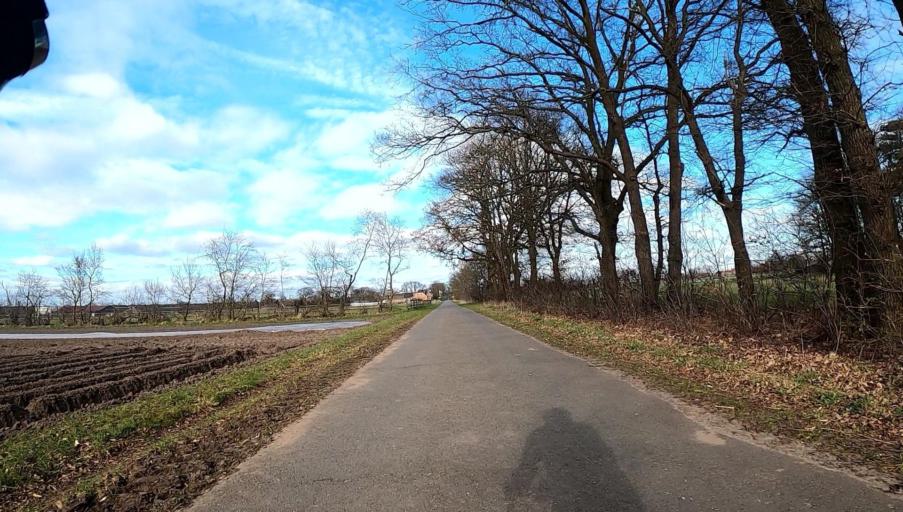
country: DE
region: Lower Saxony
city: Lindwedel
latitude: 52.6046
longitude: 9.7123
